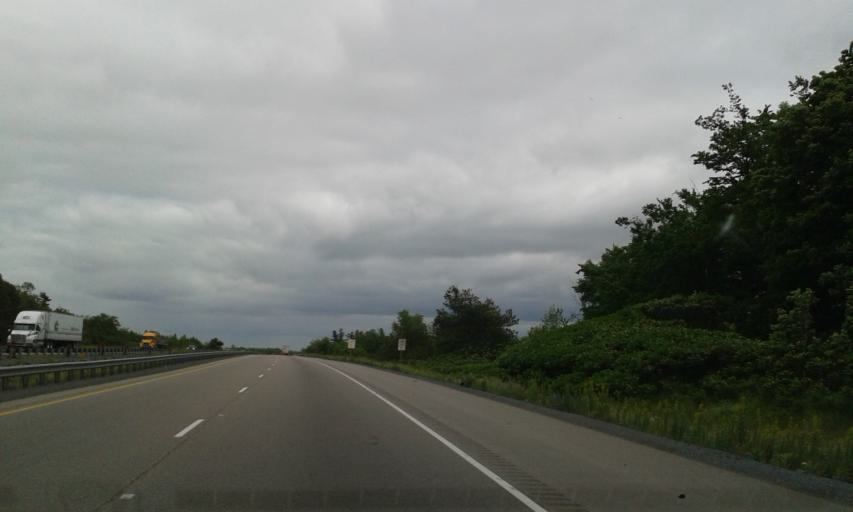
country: CA
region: Ontario
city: Kingston
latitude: 44.2827
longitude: -76.7089
